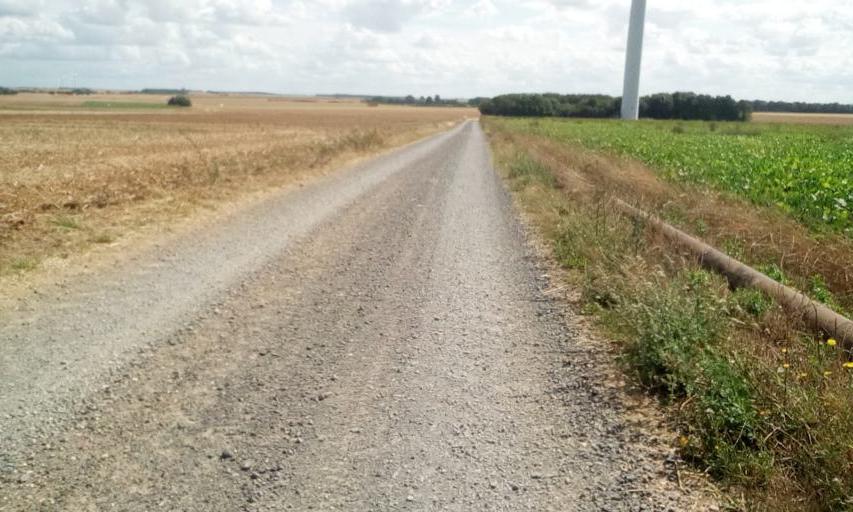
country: FR
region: Lower Normandy
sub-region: Departement du Calvados
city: Bellengreville
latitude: 49.0947
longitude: -0.2244
